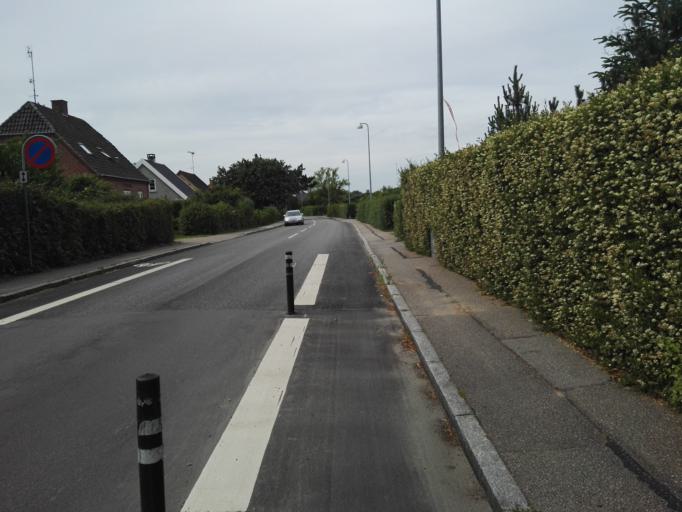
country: DK
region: Capital Region
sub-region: Hillerod Kommune
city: Skaevinge
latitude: 55.9079
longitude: 12.1587
